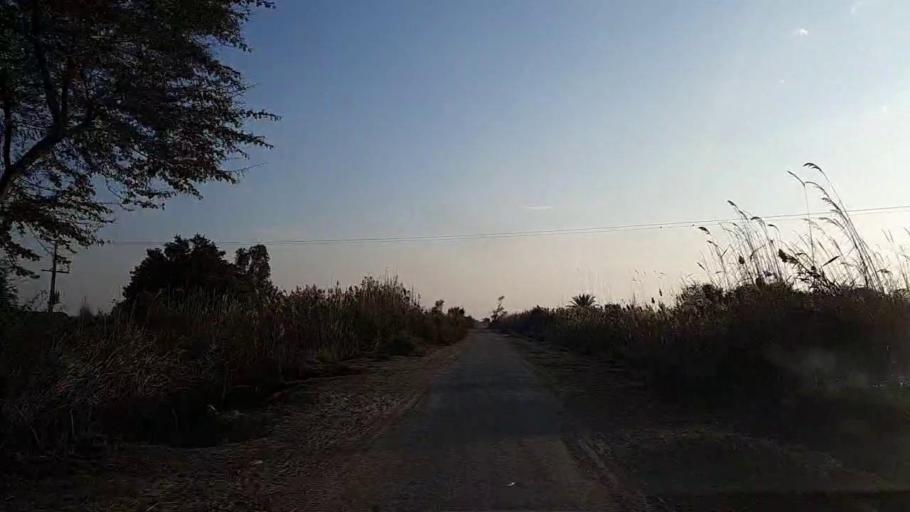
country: PK
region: Sindh
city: Sanghar
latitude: 26.2711
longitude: 68.9823
